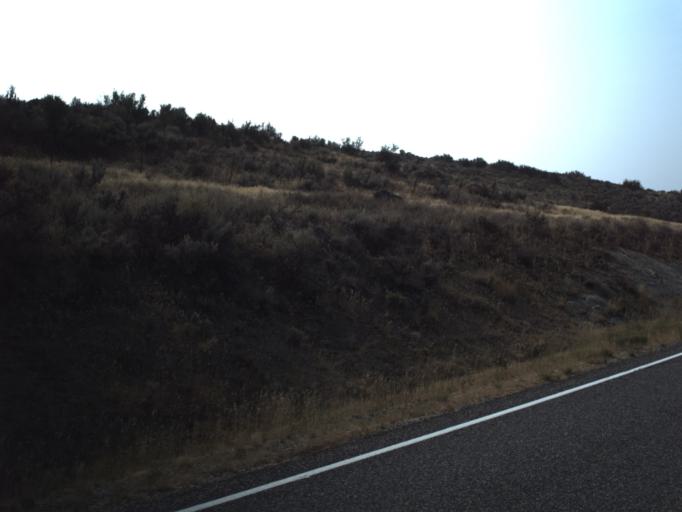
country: US
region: Utah
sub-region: Morgan County
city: Morgan
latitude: 40.9622
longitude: -111.5469
